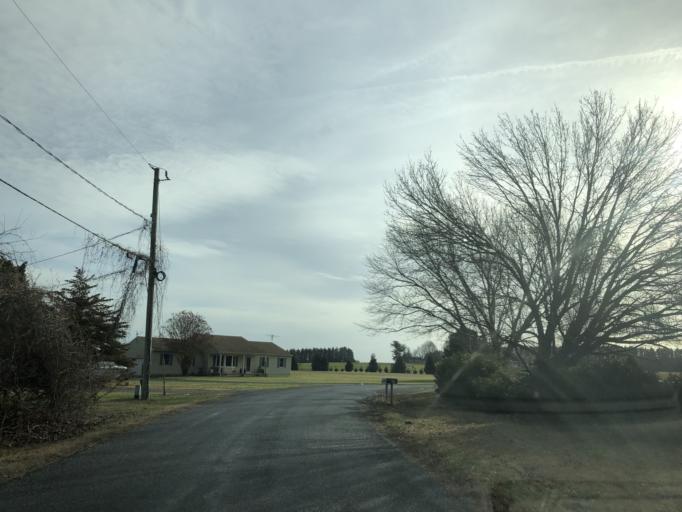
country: US
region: Delaware
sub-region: New Castle County
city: Townsend
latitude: 39.4527
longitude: -75.6337
